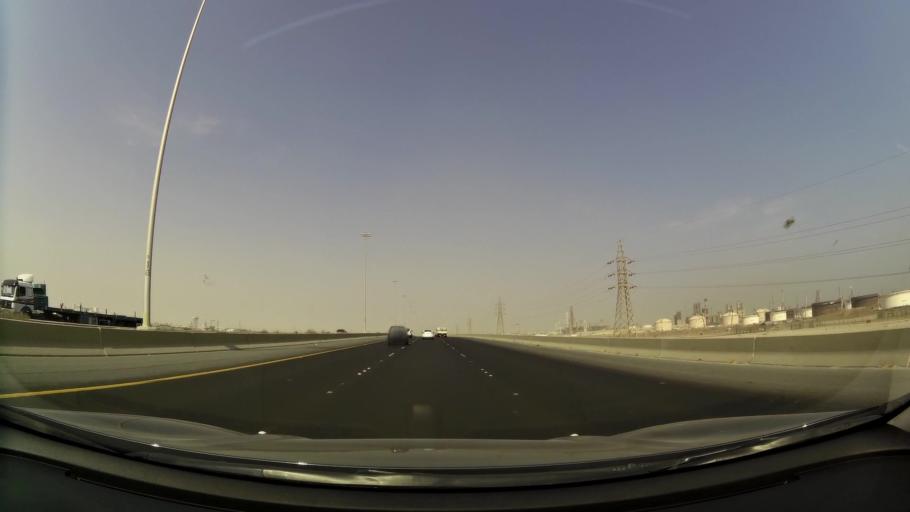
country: KW
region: Al Ahmadi
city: Al Fahahil
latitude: 29.0104
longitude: 48.1330
